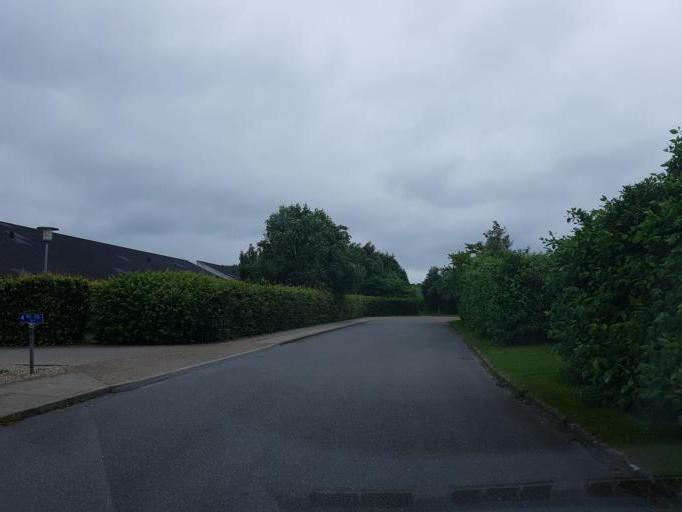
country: DK
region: South Denmark
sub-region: Varde Kommune
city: Varde
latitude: 55.6364
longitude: 8.4815
